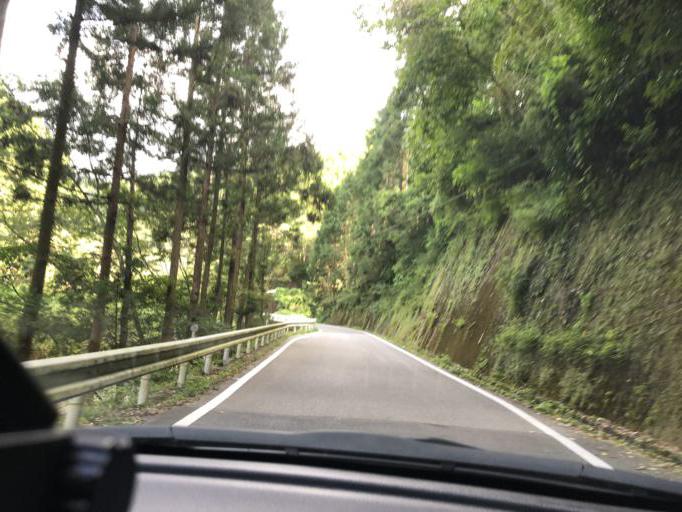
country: JP
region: Kochi
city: Kochi-shi
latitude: 33.6118
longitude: 133.5001
